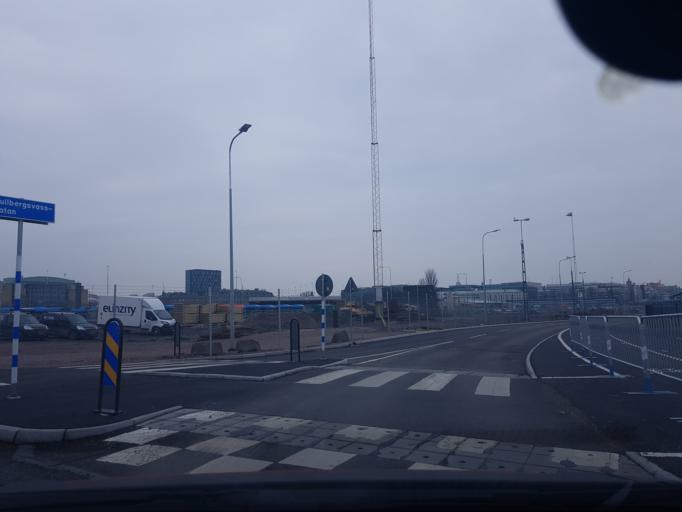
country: SE
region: Vaestra Goetaland
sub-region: Goteborg
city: Goeteborg
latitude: 57.7126
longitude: 11.9788
